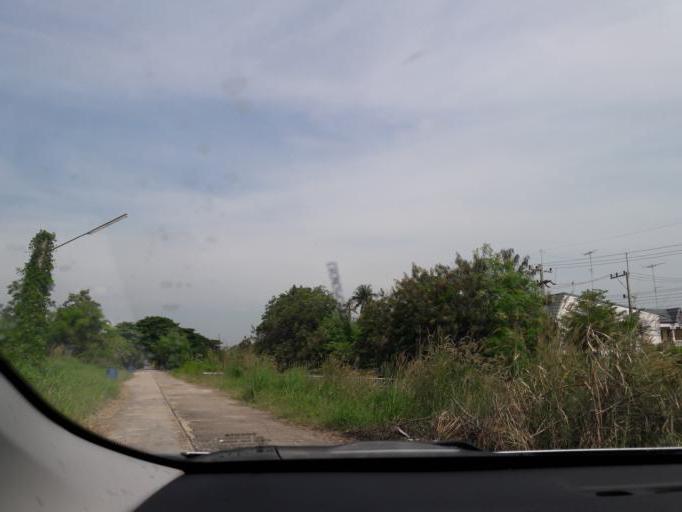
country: TH
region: Ang Thong
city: Ang Thong
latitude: 14.5735
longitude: 100.4548
